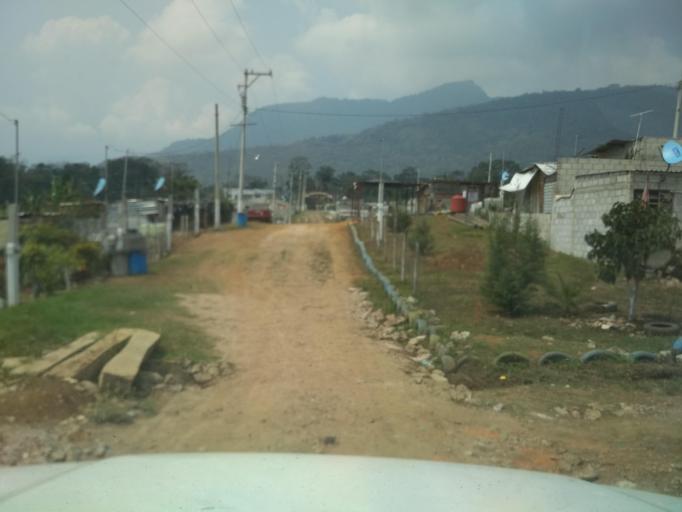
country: MX
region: Veracruz
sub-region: Cordoba
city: Fredepo
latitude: 18.8598
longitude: -96.9816
